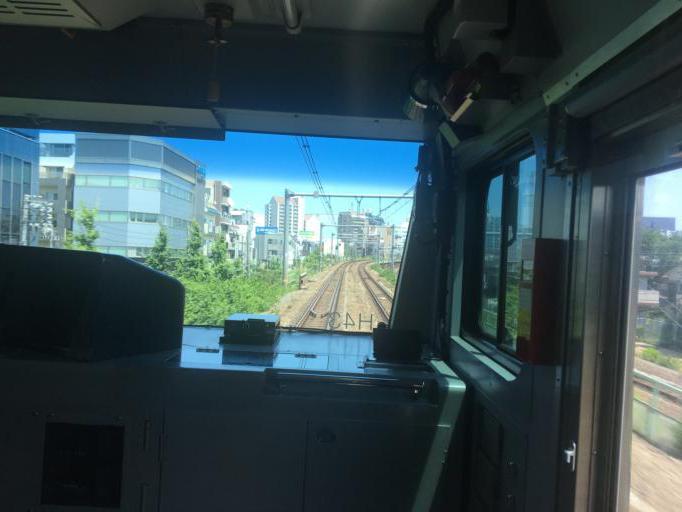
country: JP
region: Tokyo
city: Tokyo
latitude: 35.7058
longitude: 139.6900
